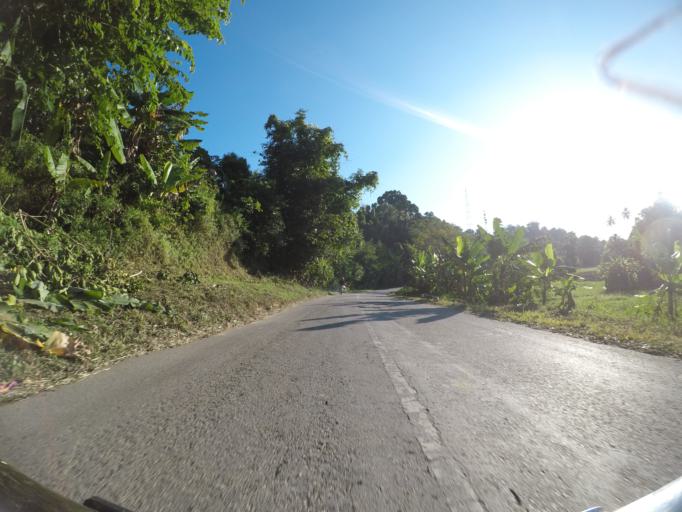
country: TZ
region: Pemba South
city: Mtambile
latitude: -5.3761
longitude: 39.6927
